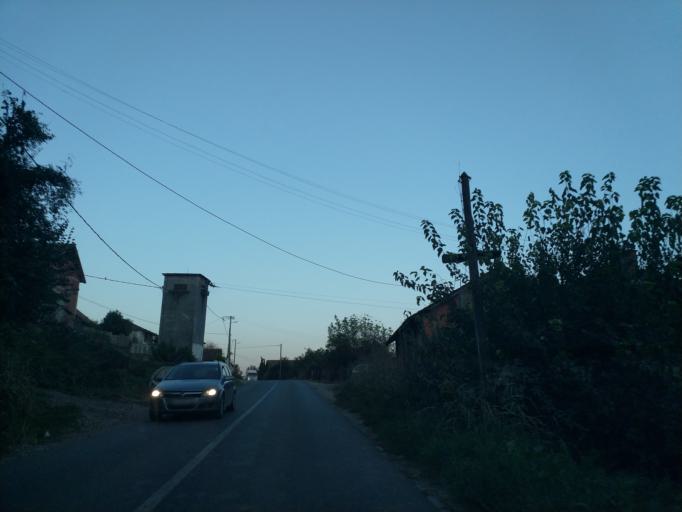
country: RS
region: Central Serbia
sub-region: Rasinski Okrug
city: Krusevac
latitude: 43.6033
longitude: 21.2198
